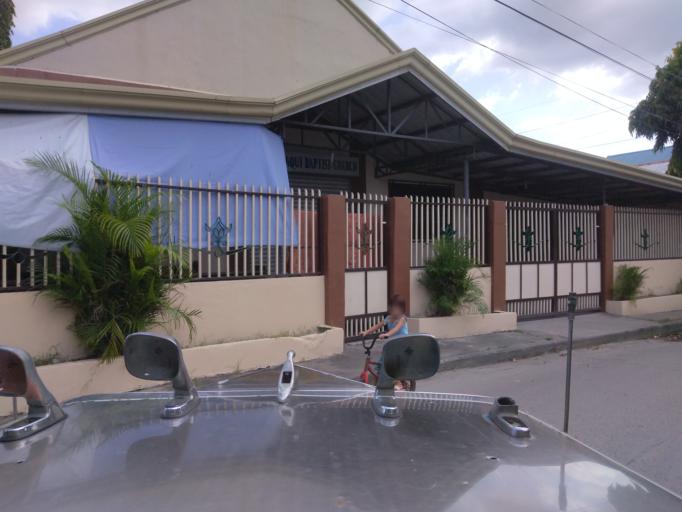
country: PH
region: Central Luzon
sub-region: Province of Pampanga
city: Pandacaqui
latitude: 15.1800
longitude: 120.6482
